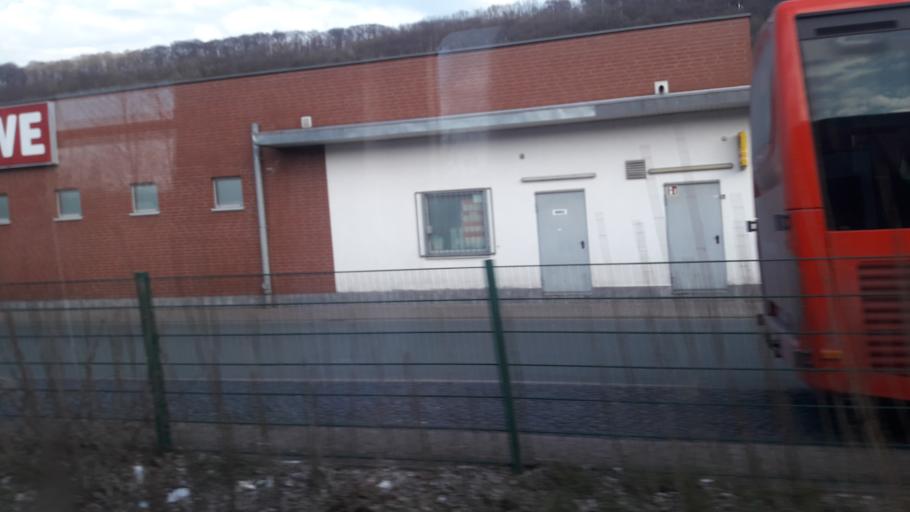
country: DE
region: North Rhine-Westphalia
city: Marsberg
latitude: 51.4644
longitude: 8.8570
